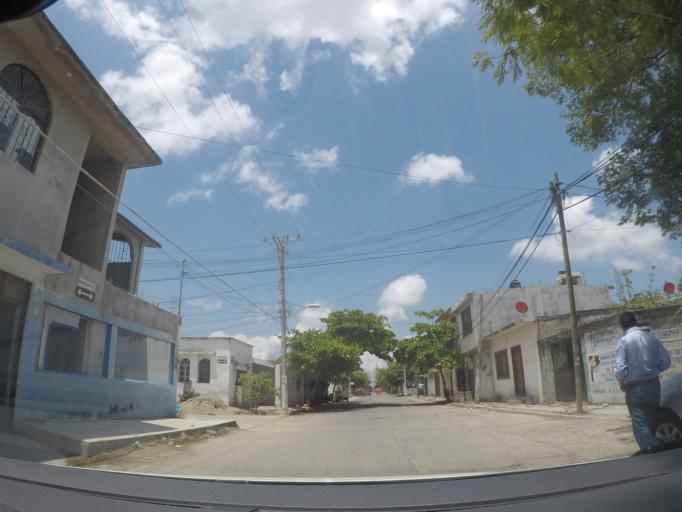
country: MX
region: Oaxaca
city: Juchitan de Zaragoza
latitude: 16.4412
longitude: -95.0105
